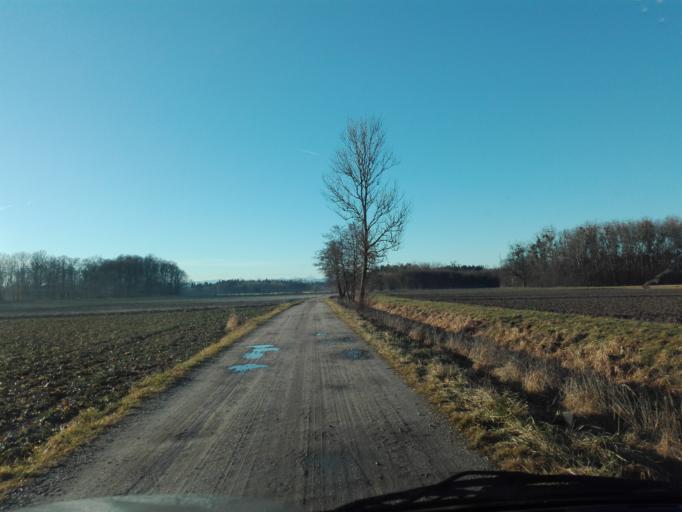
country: AT
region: Upper Austria
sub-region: Politischer Bezirk Perg
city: Perg
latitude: 48.2254
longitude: 14.6835
